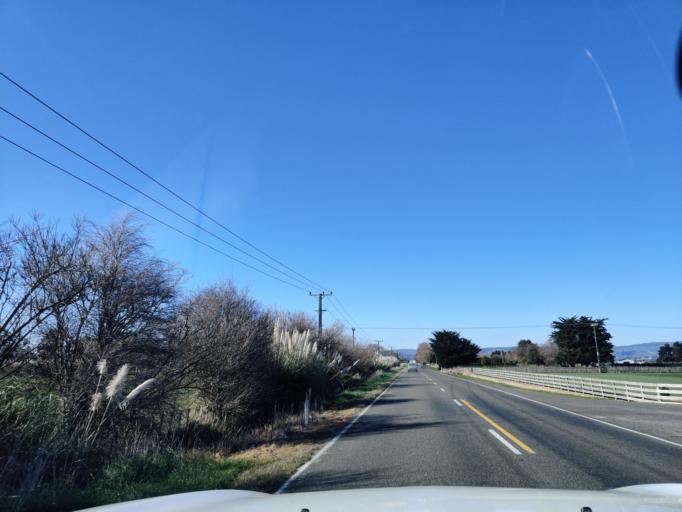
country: NZ
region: Manawatu-Wanganui
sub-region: Palmerston North City
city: Palmerston North
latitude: -40.3121
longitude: 175.5923
